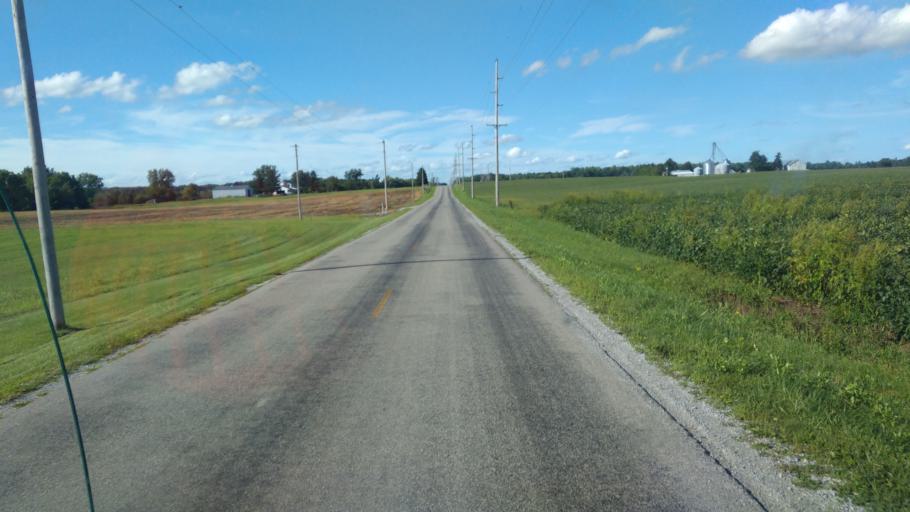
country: US
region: Ohio
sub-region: Hardin County
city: Kenton
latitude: 40.6962
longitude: -83.6538
